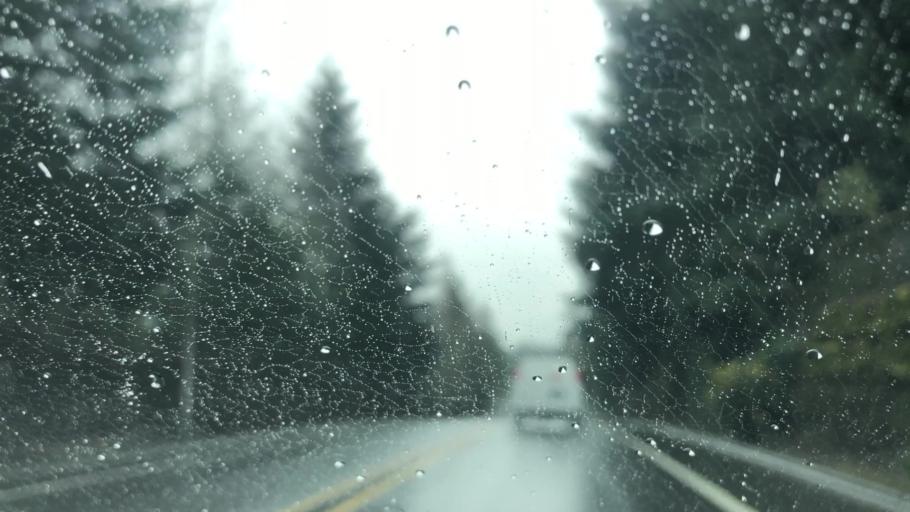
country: US
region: Oregon
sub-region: Washington County
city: Cedar Mill
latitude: 45.5251
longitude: -122.7929
